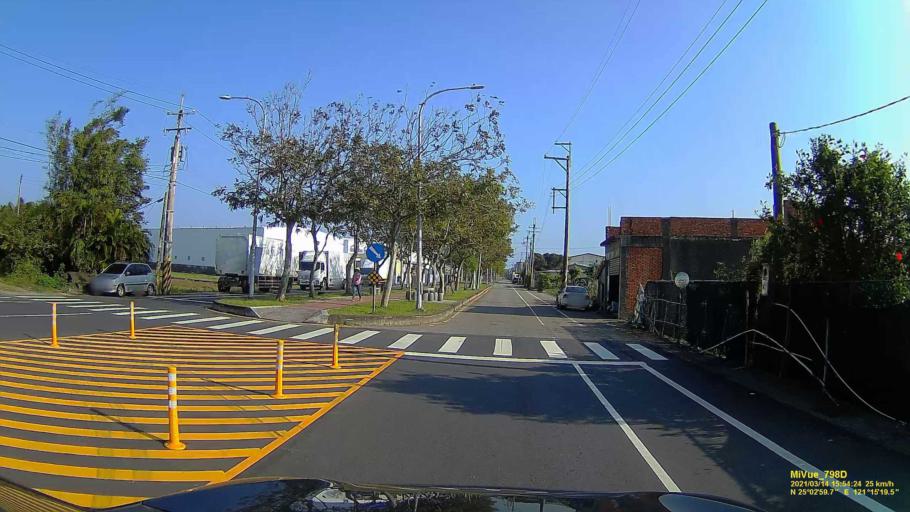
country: TW
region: Taiwan
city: Taoyuan City
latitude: 25.0497
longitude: 121.2555
